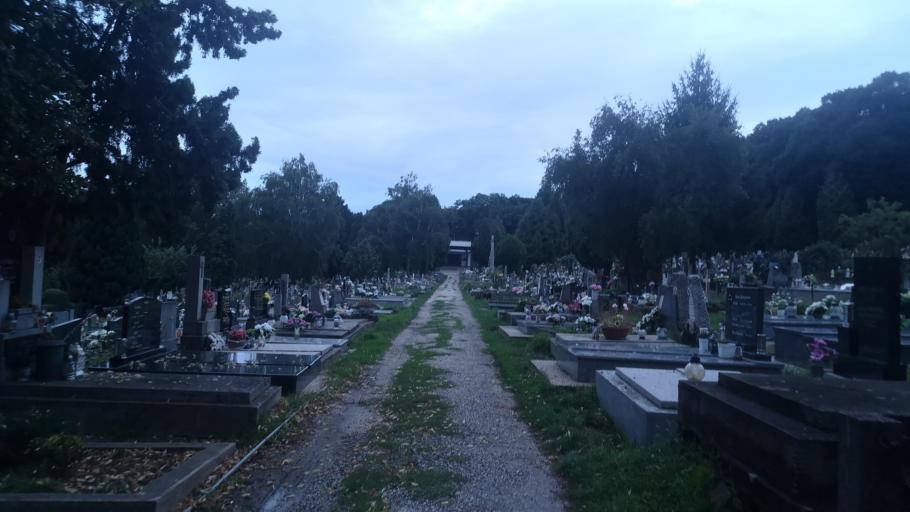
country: SK
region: Nitriansky
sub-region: Okres Nitra
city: Nitra
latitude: 48.3052
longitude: 18.0708
